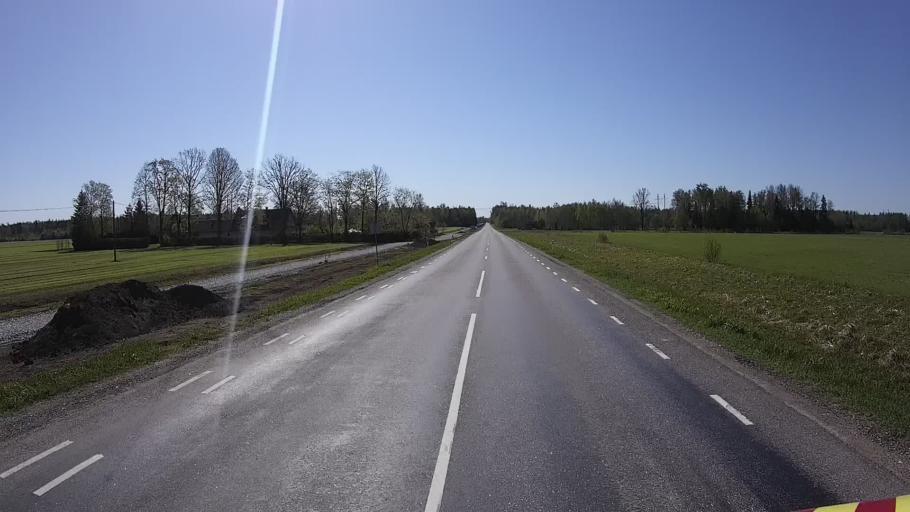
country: EE
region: Paernumaa
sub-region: Tootsi vald
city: Tootsi
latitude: 58.5036
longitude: 24.7970
